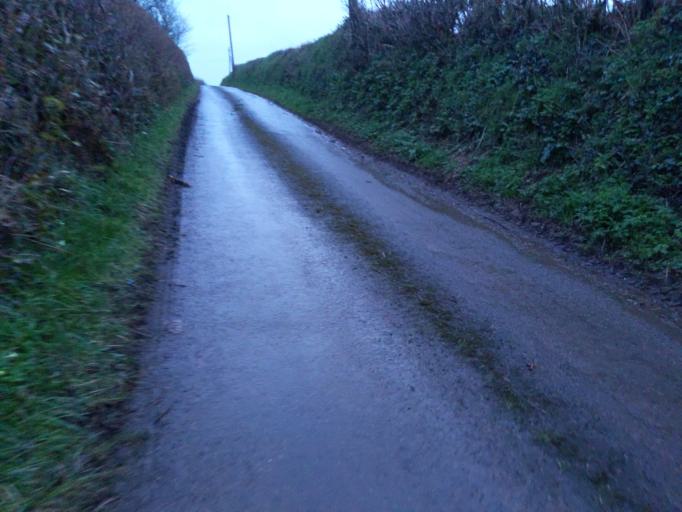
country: GB
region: England
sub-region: Devon
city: Yealmpton
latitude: 50.3337
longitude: -4.0154
